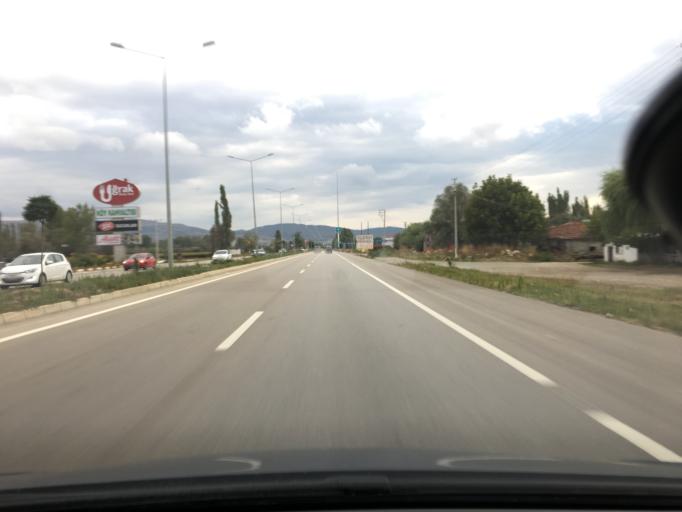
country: TR
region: Afyonkarahisar
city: Sincanli
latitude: 38.7636
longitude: 30.3650
